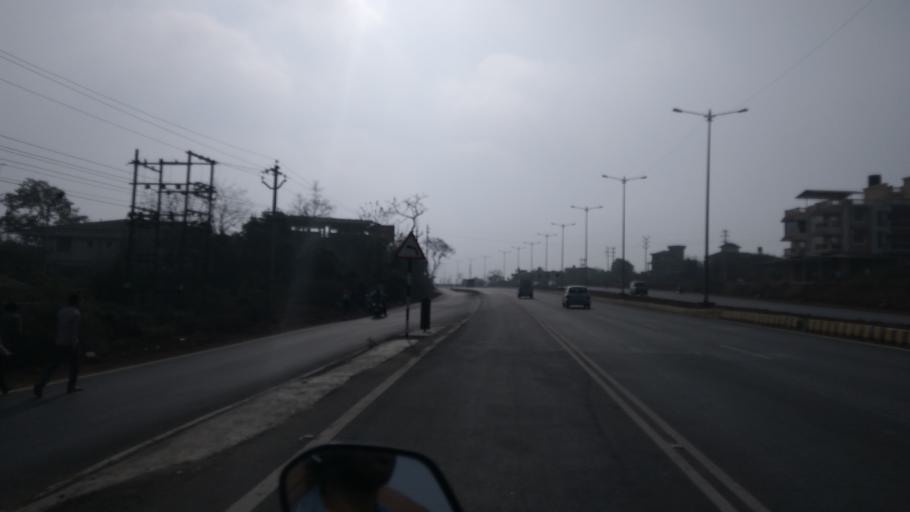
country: IN
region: Goa
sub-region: North Goa
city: Bambolim
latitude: 15.4950
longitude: 73.8812
